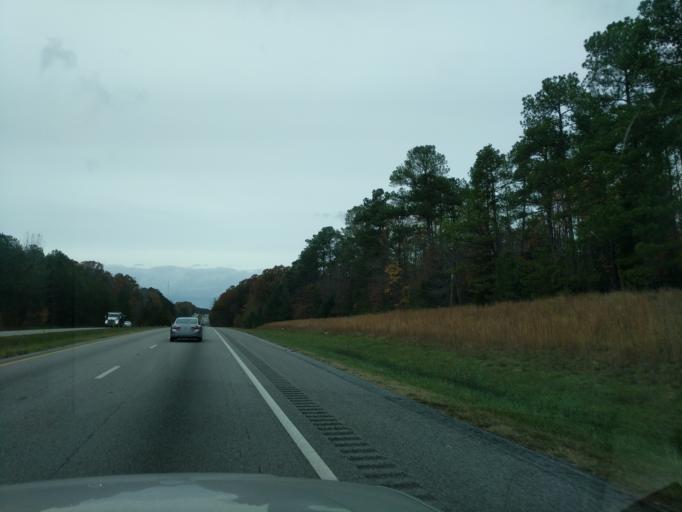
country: US
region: South Carolina
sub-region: Laurens County
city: Joanna
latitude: 34.4553
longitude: -81.7867
